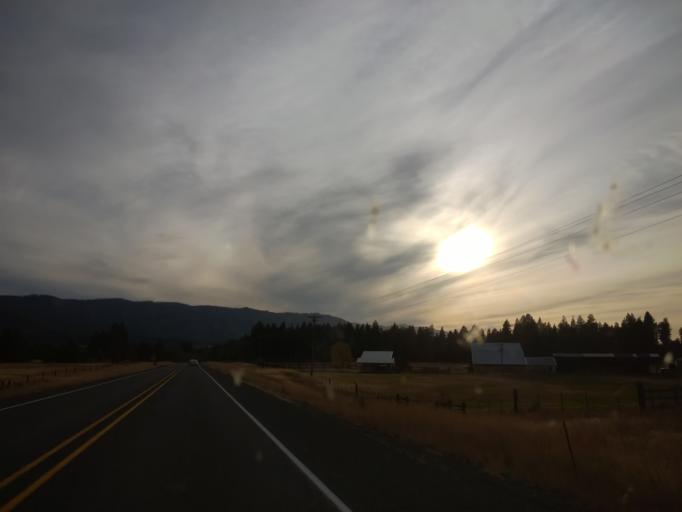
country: US
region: Washington
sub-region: Kittitas County
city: Cle Elum
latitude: 47.1801
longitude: -120.8379
